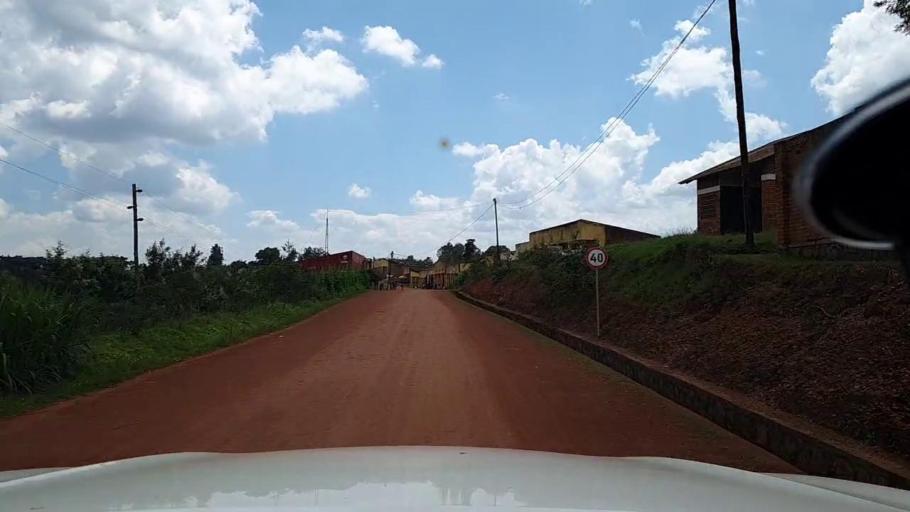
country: RW
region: Kigali
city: Kigali
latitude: -1.8032
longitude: 29.8421
